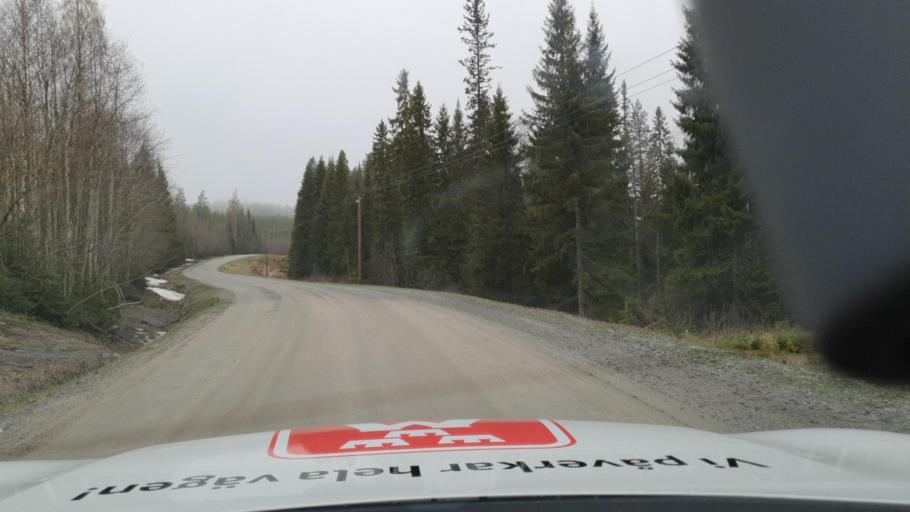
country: SE
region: Vaesterbotten
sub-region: Nordmalings Kommun
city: Nordmaling
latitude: 63.7539
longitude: 19.4971
